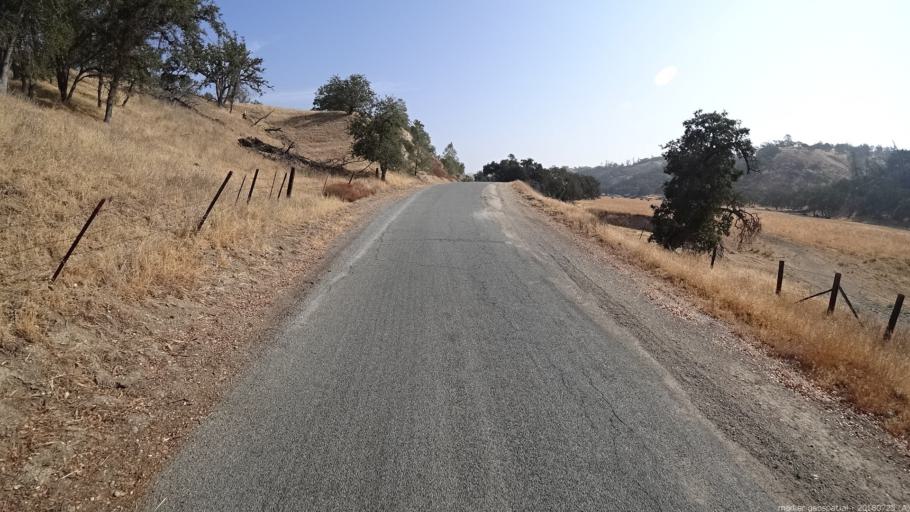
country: US
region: California
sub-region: San Luis Obispo County
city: San Miguel
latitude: 35.8167
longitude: -120.5210
